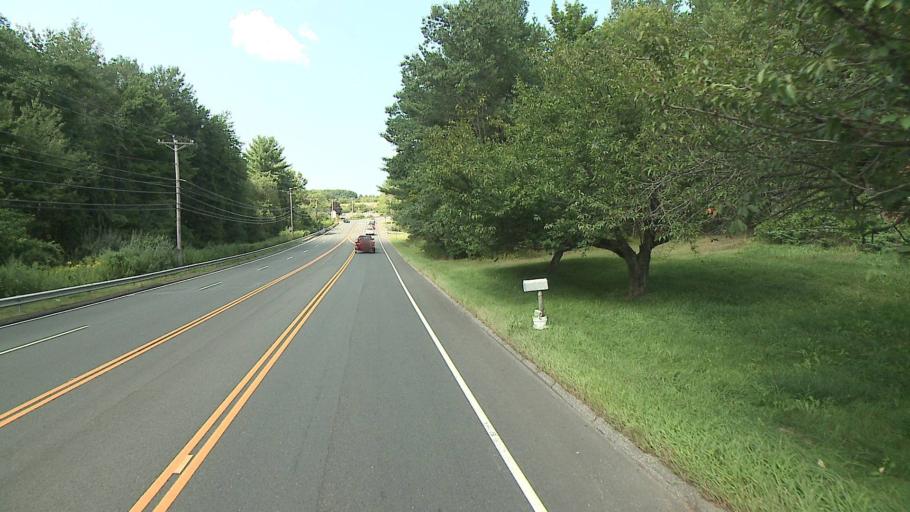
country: US
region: Connecticut
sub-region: Fairfield County
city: Newtown
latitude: 41.3696
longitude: -73.2712
